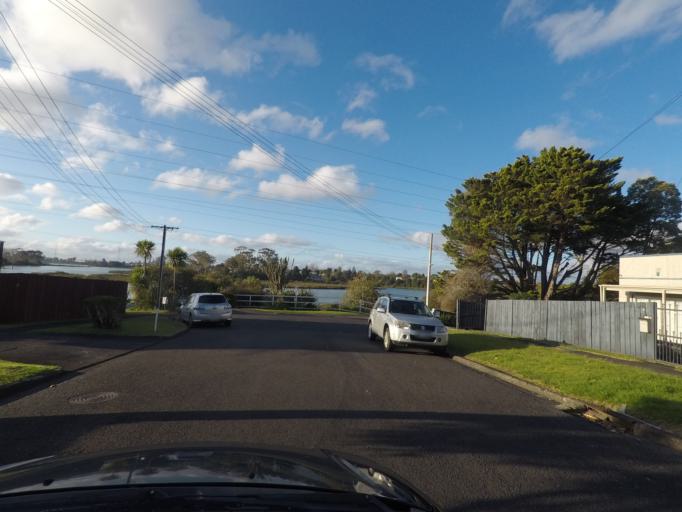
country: NZ
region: Auckland
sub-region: Auckland
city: Waitakere
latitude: -36.8999
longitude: 174.6736
